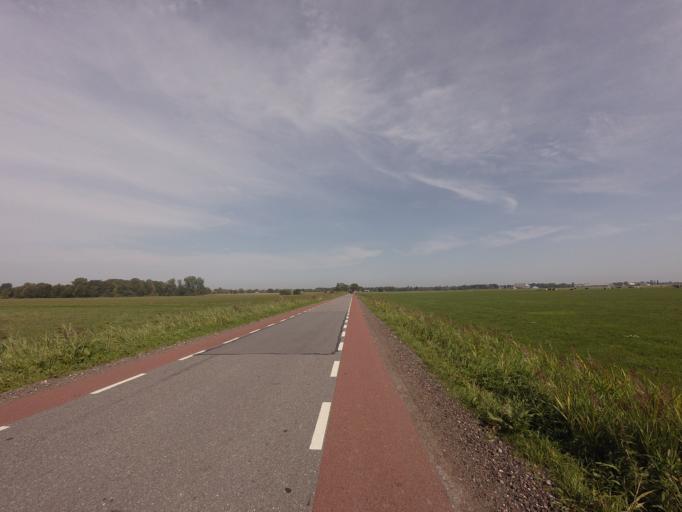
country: NL
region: Groningen
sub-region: Gemeente Leek
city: Leek
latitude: 53.2116
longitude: 6.3461
